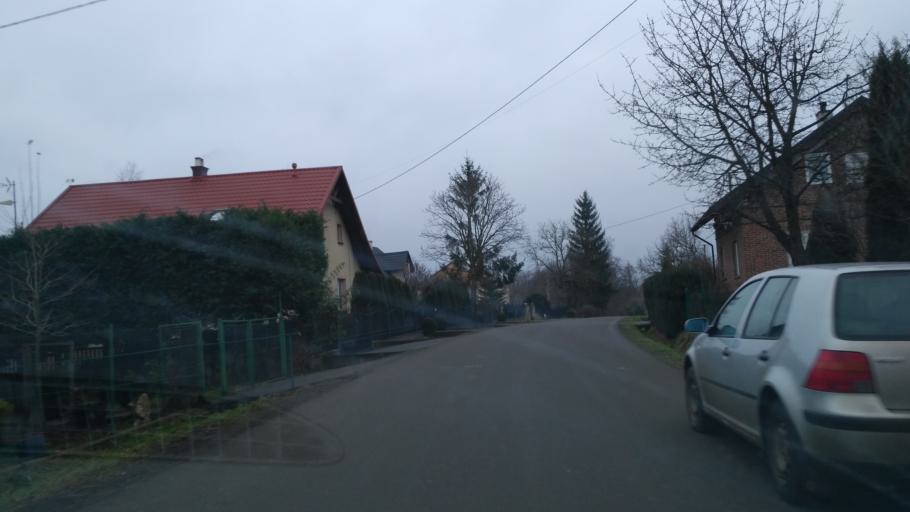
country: PL
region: Subcarpathian Voivodeship
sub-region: Powiat jaroslawski
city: Pruchnik
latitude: 49.9299
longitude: 22.5355
